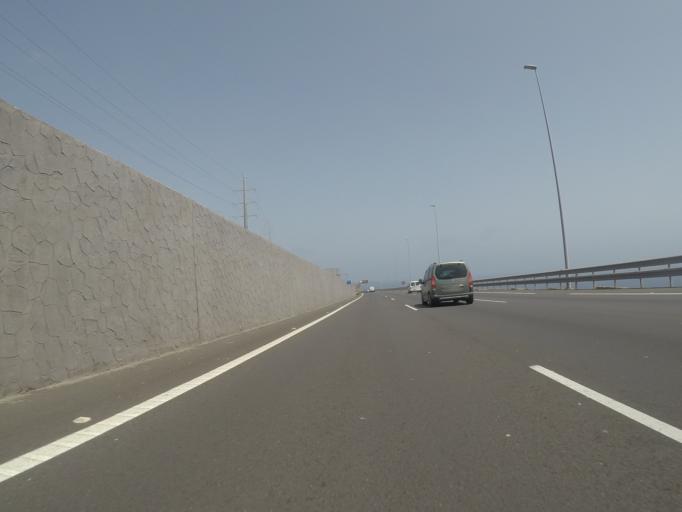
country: ES
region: Canary Islands
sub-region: Provincia de Santa Cruz de Tenerife
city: Santa Cruz de Tenerife
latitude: 28.4326
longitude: -16.2885
